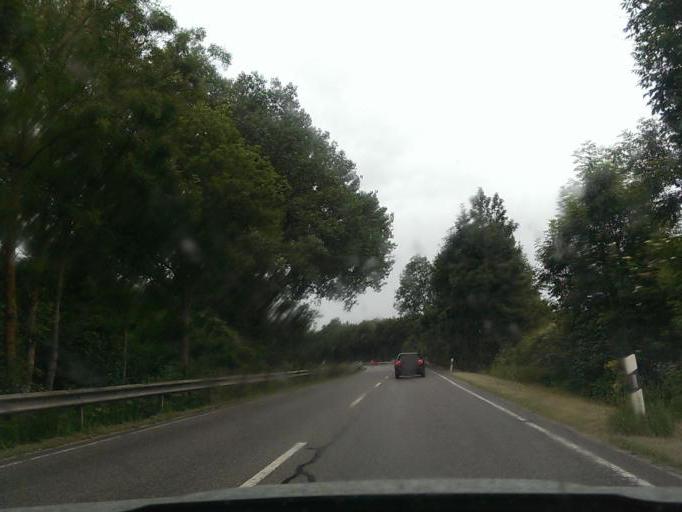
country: DE
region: Bavaria
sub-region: Regierungsbezirk Mittelfranken
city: Greding
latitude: 48.9995
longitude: 11.3847
